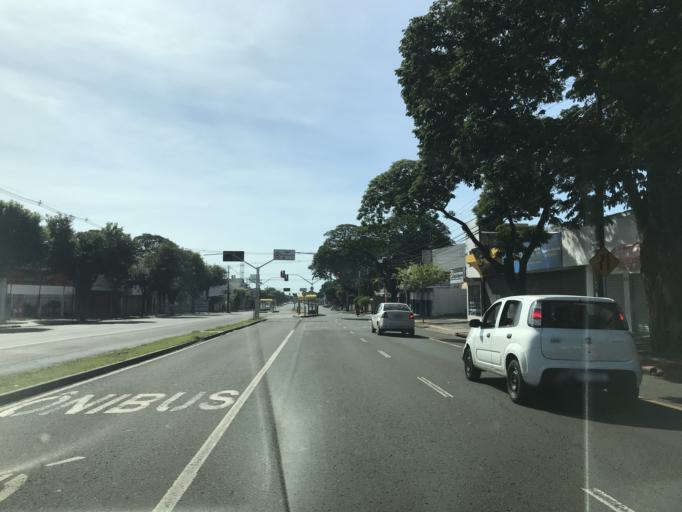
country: BR
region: Parana
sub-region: Maringa
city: Maringa
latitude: -23.4062
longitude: -51.9298
